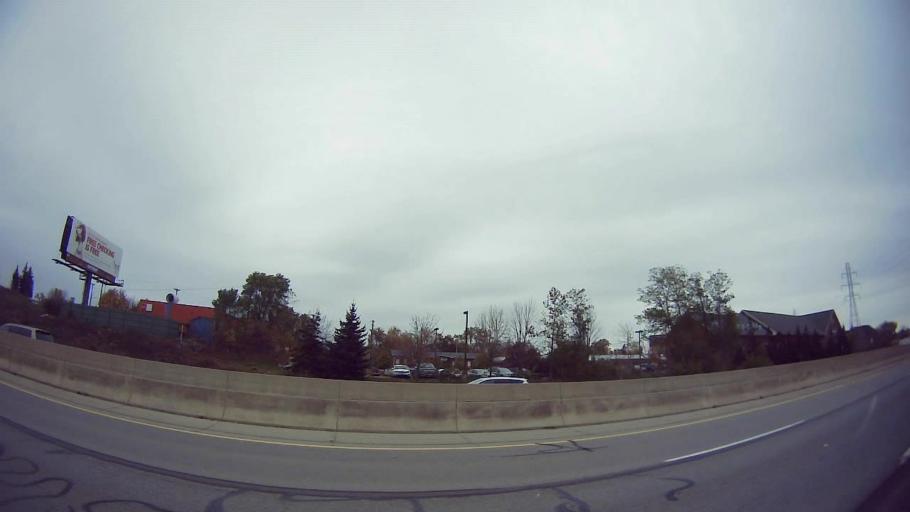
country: US
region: Michigan
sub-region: Oakland County
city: Sylvan Lake
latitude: 42.6182
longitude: -83.3203
